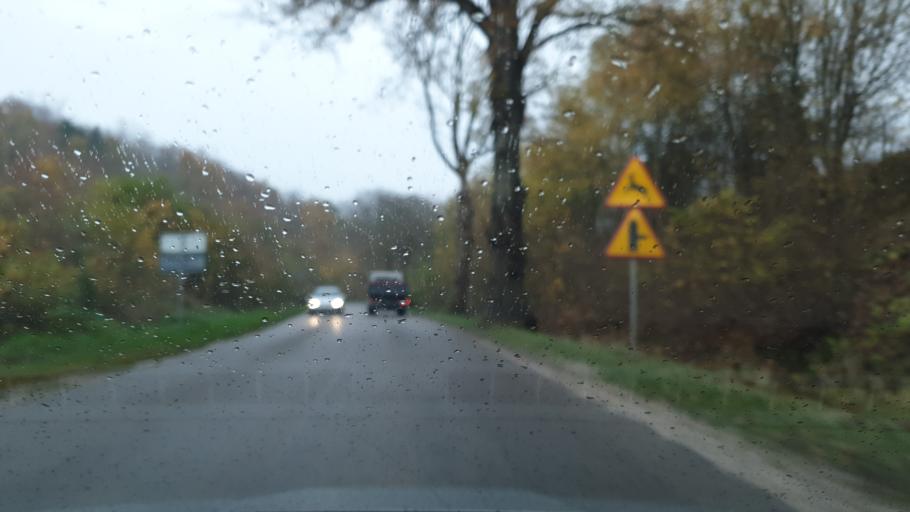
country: PL
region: Pomeranian Voivodeship
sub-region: Powiat pucki
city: Krokowa
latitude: 54.7713
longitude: 18.2185
